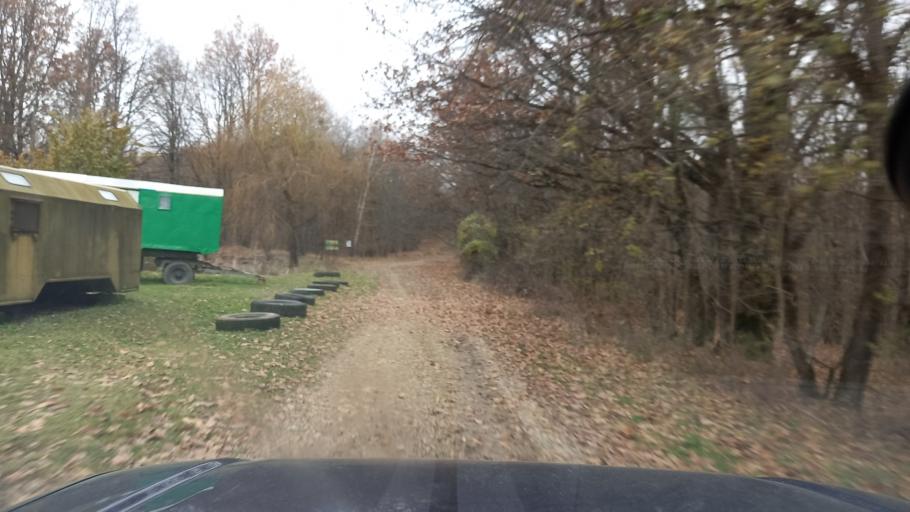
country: RU
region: Krasnodarskiy
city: Goryachiy Klyuch
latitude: 44.5116
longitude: 39.2938
